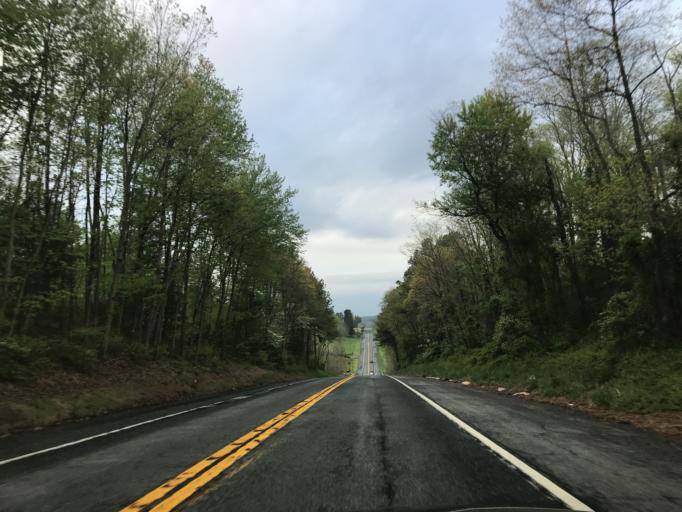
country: US
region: Maryland
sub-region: Harford County
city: Jarrettsville
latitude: 39.6651
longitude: -76.4251
